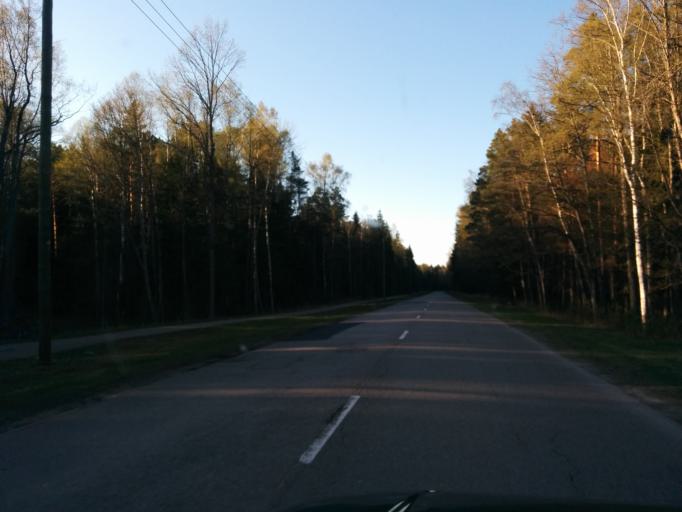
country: LV
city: Tireli
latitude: 56.9551
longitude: 23.5222
